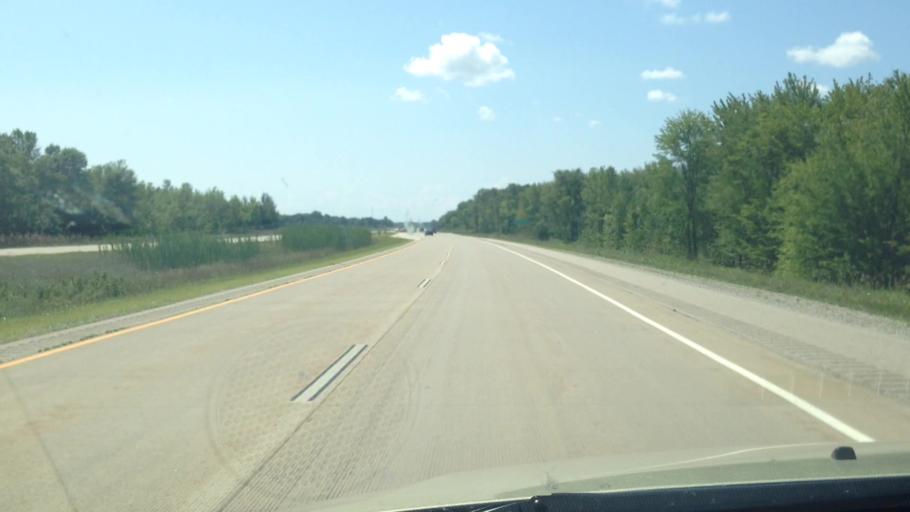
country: US
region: Wisconsin
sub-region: Oconto County
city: Oconto
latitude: 44.9648
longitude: -87.8722
